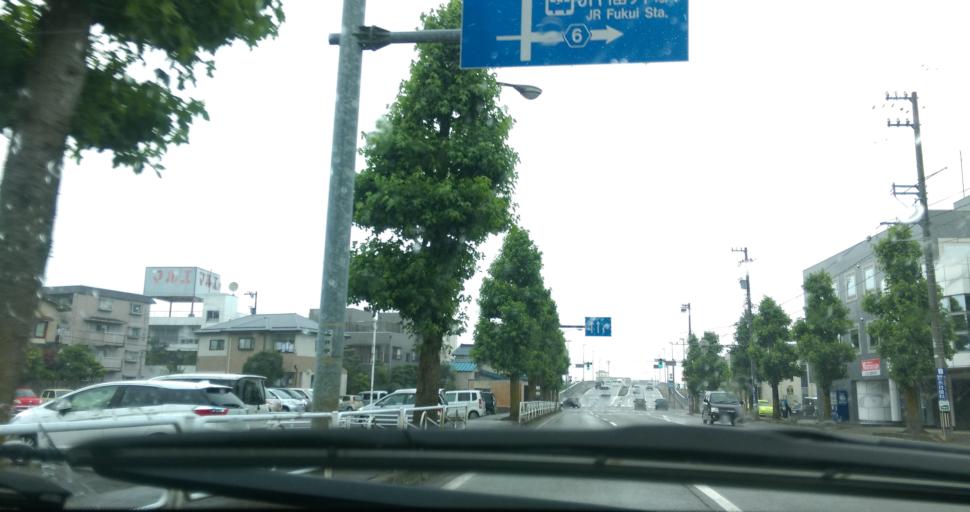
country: JP
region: Fukui
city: Fukui-shi
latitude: 36.0605
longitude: 136.1973
